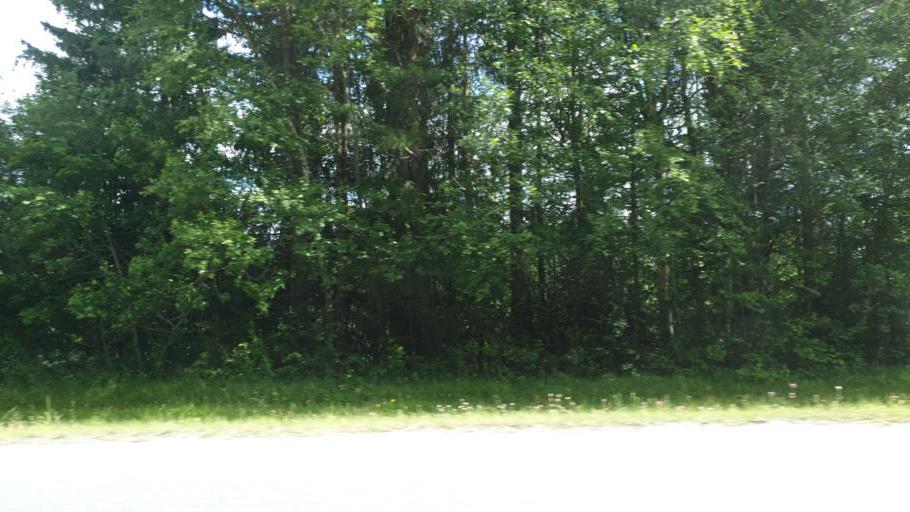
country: NO
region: Sor-Trondelag
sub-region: Rennebu
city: Berkak
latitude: 62.7124
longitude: 9.9593
